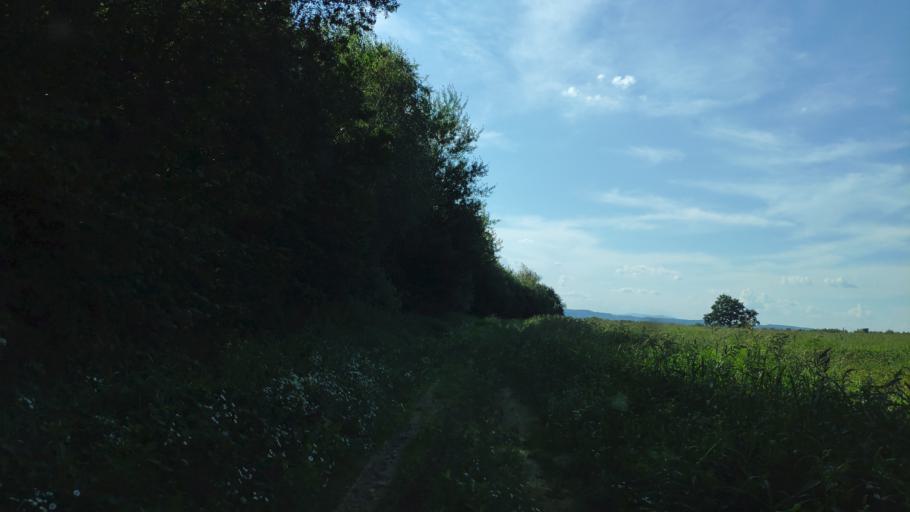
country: SK
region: Presovsky
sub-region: Okres Presov
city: Presov
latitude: 48.9058
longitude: 21.2957
